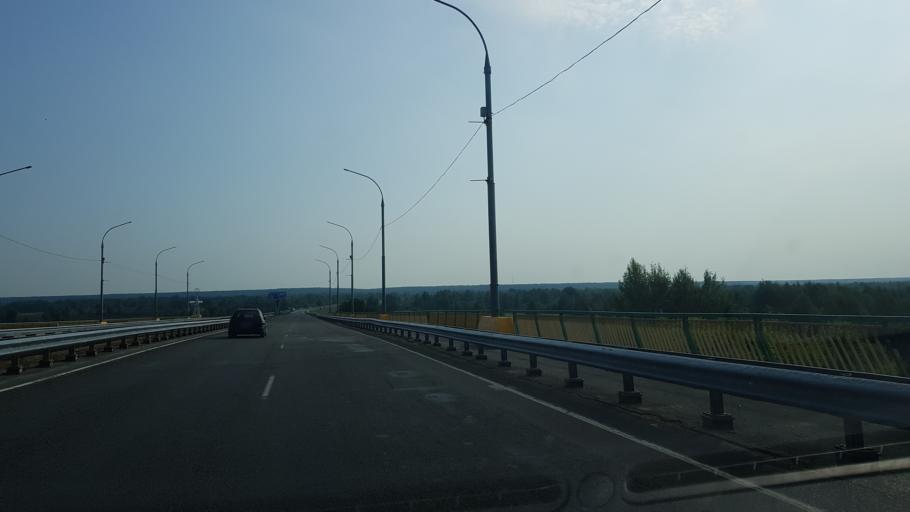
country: BY
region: Mogilev
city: Babruysk
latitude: 53.1619
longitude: 29.2430
